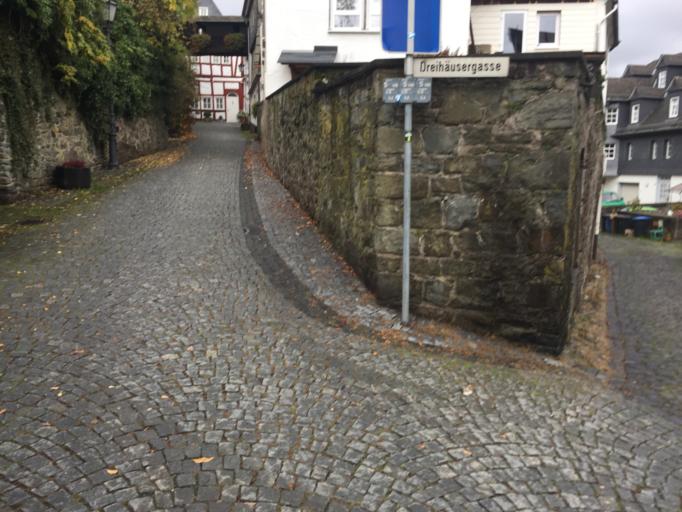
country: DE
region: Hesse
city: Herborn
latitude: 50.6832
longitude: 8.3020
